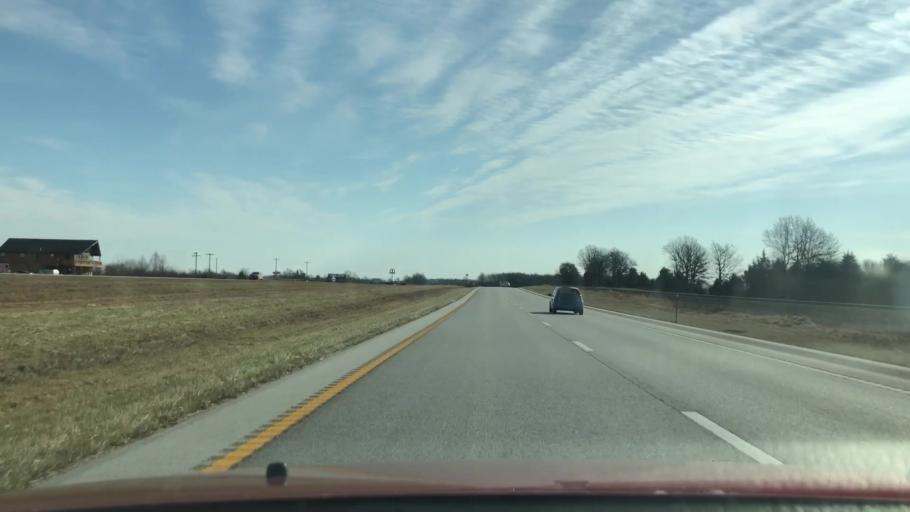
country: US
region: Missouri
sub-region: Webster County
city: Seymour
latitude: 37.1601
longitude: -92.7934
